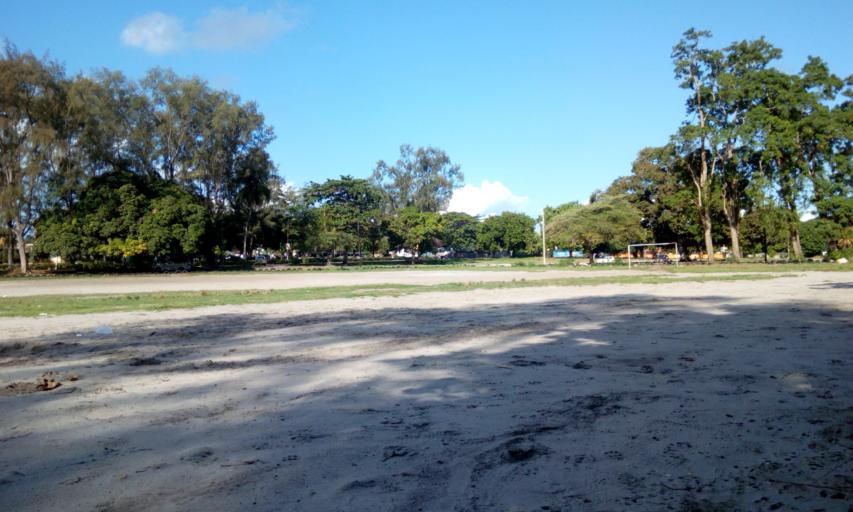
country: TZ
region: Zanzibar Urban/West
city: Zanzibar
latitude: -6.1735
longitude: 39.1950
